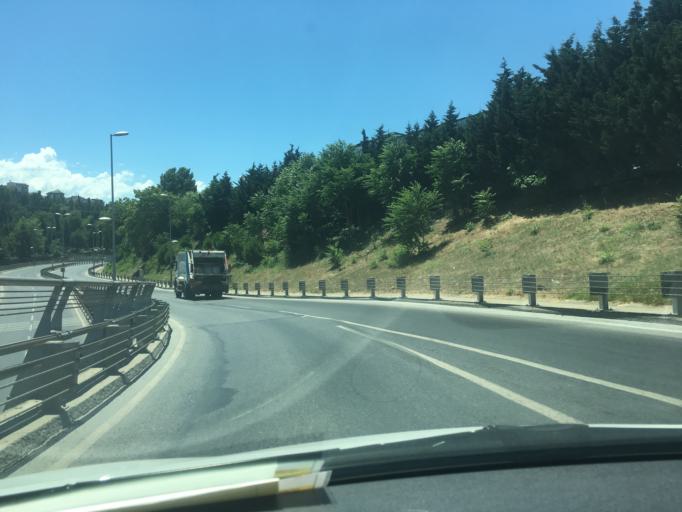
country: TR
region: Istanbul
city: Sisli
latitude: 41.0518
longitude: 28.9694
